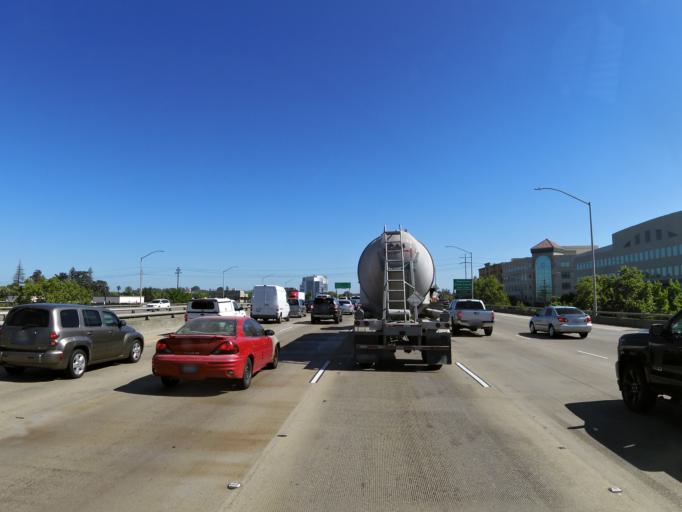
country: US
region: California
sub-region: Sacramento County
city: Sacramento
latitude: 38.5630
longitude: -121.4715
